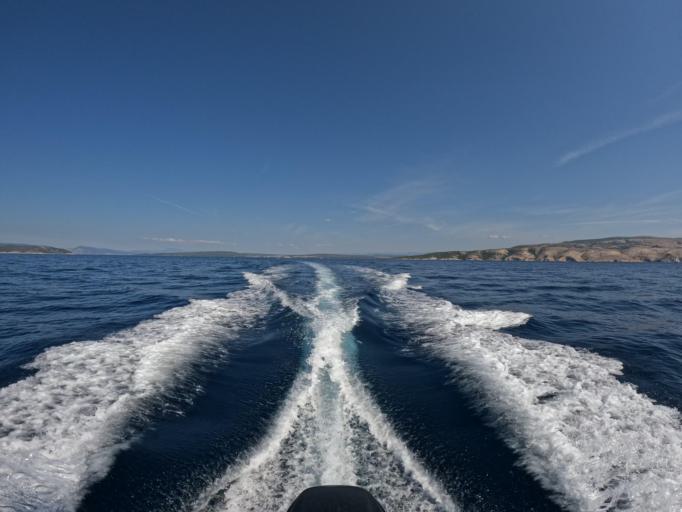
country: HR
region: Primorsko-Goranska
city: Punat
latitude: 44.9450
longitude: 14.6148
